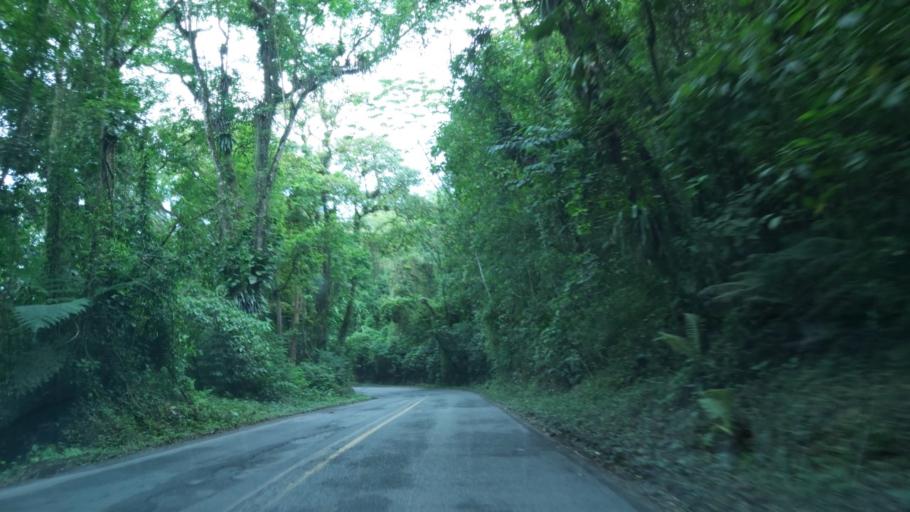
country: BR
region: Sao Paulo
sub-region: Juquia
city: Juquia
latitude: -24.0767
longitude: -47.6041
